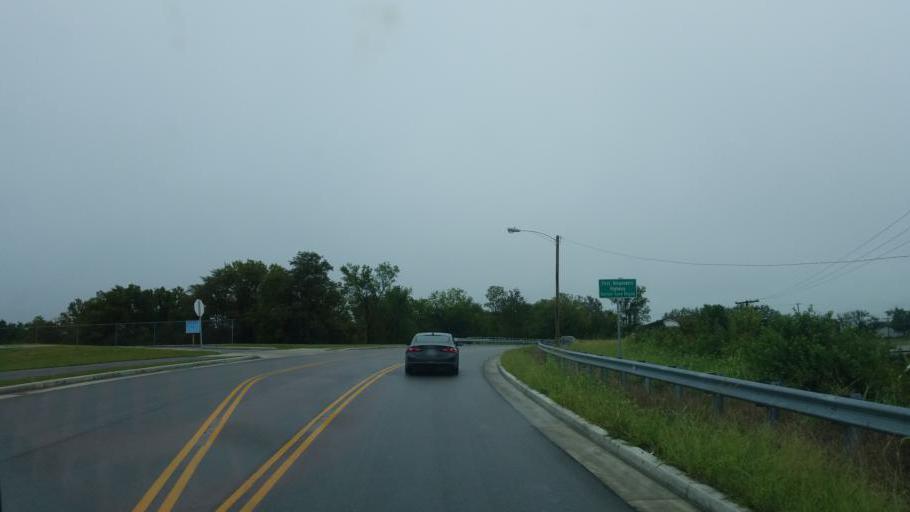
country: US
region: Ohio
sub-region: Brown County
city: Aberdeen
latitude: 38.6395
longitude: -83.7839
